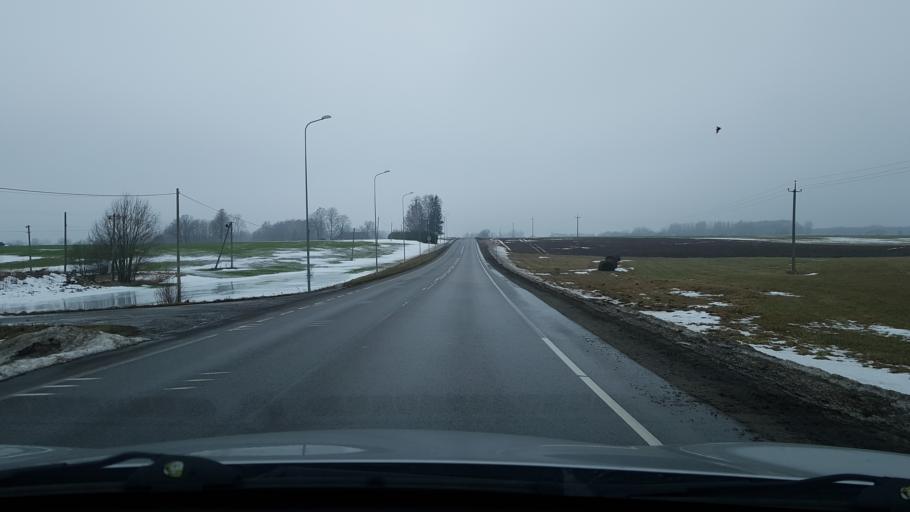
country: EE
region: Viljandimaa
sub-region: Viiratsi vald
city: Viiratsi
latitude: 58.2449
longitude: 25.8528
